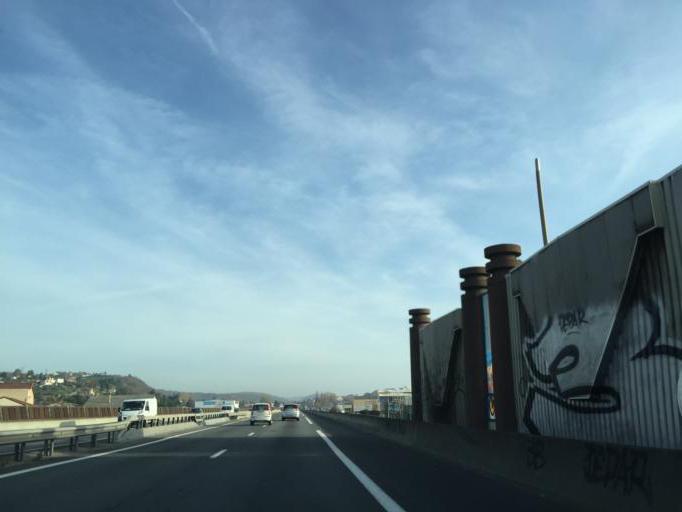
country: FR
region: Rhone-Alpes
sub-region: Departement de la Loire
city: La Grand-Croix
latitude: 45.4977
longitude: 4.5588
